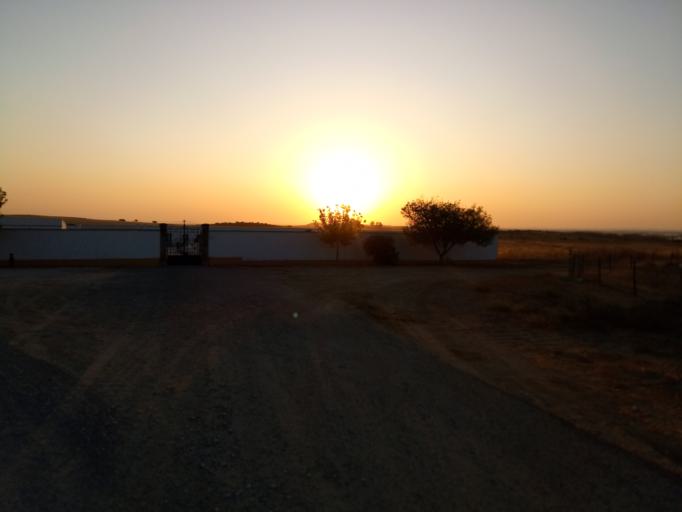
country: PT
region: Evora
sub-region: Reguengos de Monsaraz
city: Reguengos de Monsaraz
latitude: 38.3691
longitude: -7.4641
